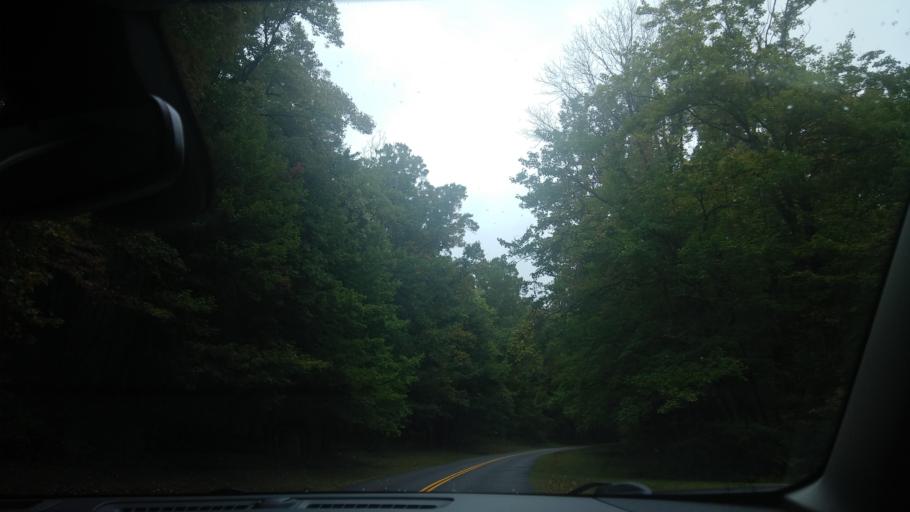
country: US
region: North Carolina
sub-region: Mitchell County
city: Spruce Pine
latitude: 35.9050
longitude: -81.9780
